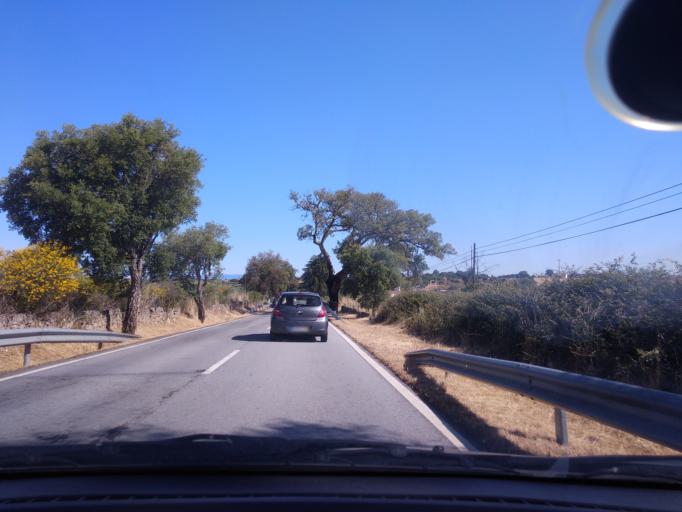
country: PT
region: Portalegre
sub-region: Nisa
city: Nisa
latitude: 39.4962
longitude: -7.6421
